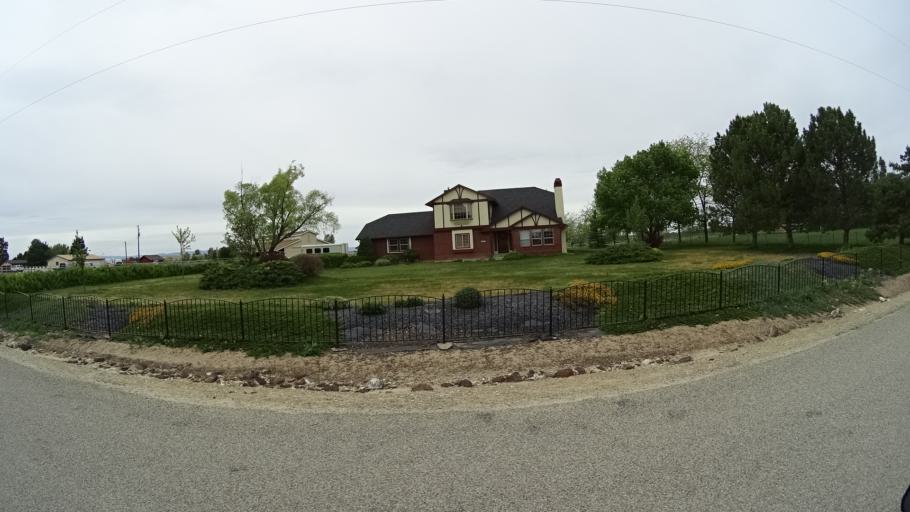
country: US
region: Idaho
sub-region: Ada County
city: Kuna
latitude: 43.4997
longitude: -116.3394
